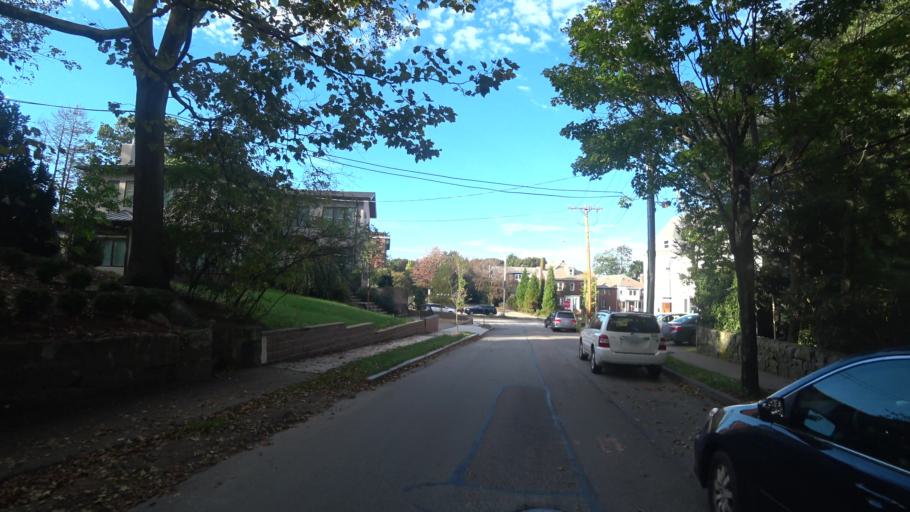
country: US
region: Massachusetts
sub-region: Norfolk County
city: Brookline
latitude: 42.3292
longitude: -71.1284
